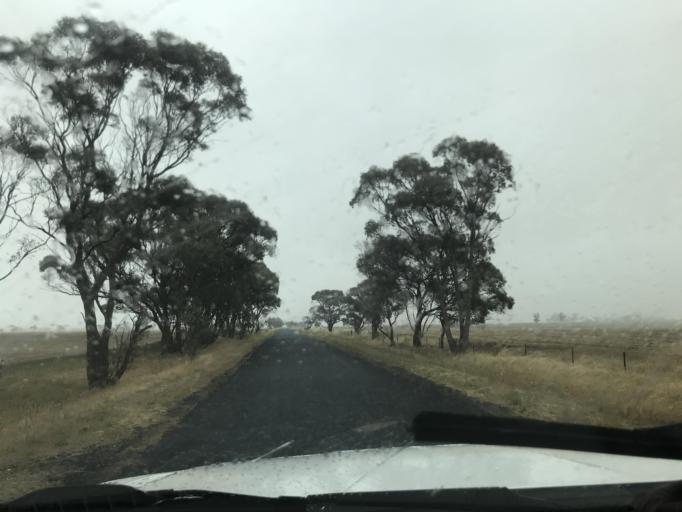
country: AU
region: South Australia
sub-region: Tatiara
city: Bordertown
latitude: -36.3141
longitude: 141.1551
